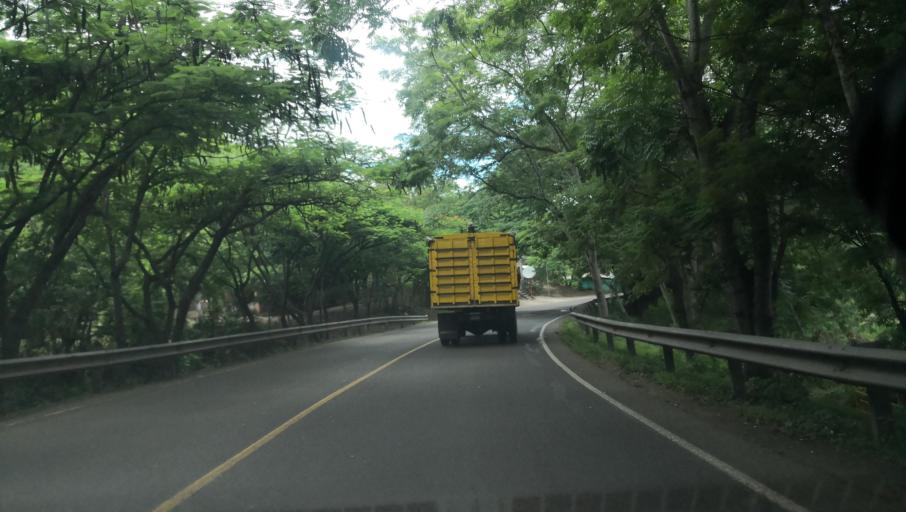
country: NI
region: Madriz
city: Yalaguina
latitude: 13.4673
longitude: -86.4734
